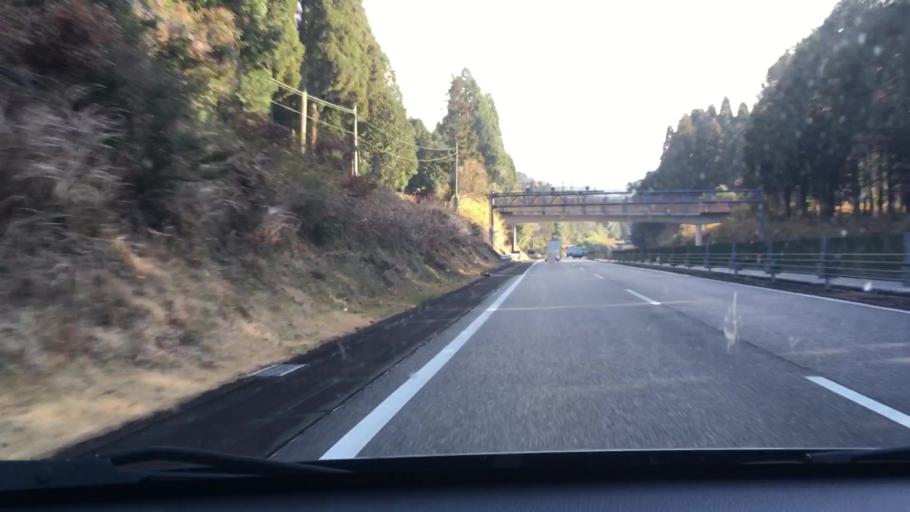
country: JP
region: Kagoshima
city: Okuchi-shinohara
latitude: 32.0023
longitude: 130.7569
